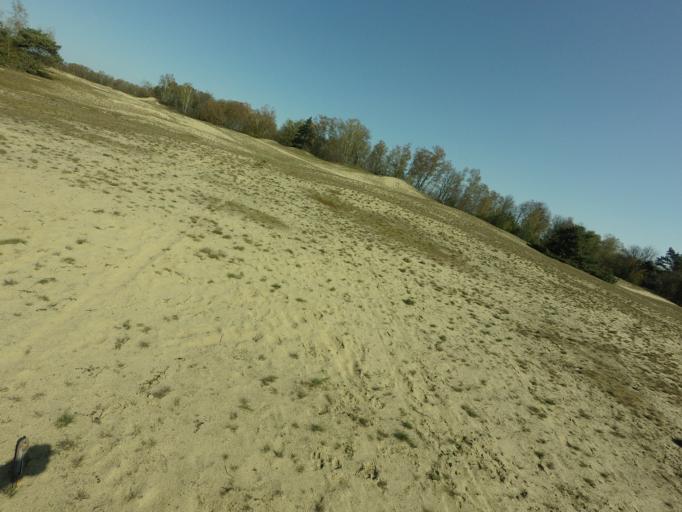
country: NL
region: Limburg
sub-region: Gemeente Bergen
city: Wellerlooi
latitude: 51.6003
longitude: 6.0709
